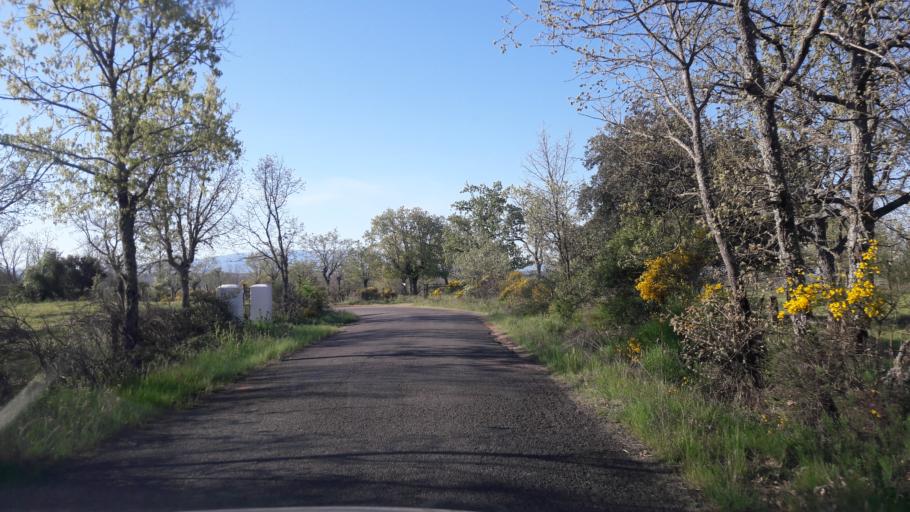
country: ES
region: Castille and Leon
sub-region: Provincia de Salamanca
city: Monleon
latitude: 40.6070
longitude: -5.8446
